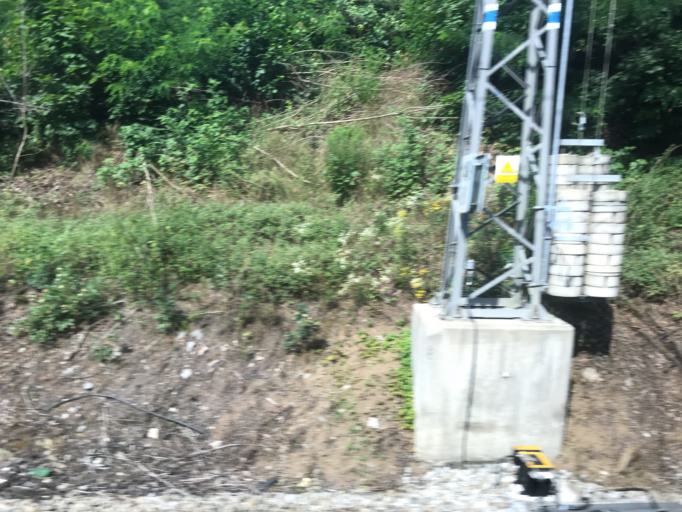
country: CZ
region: Central Bohemia
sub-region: Okres Praha-Vychod
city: Mnichovice
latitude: 49.8930
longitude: 14.7295
